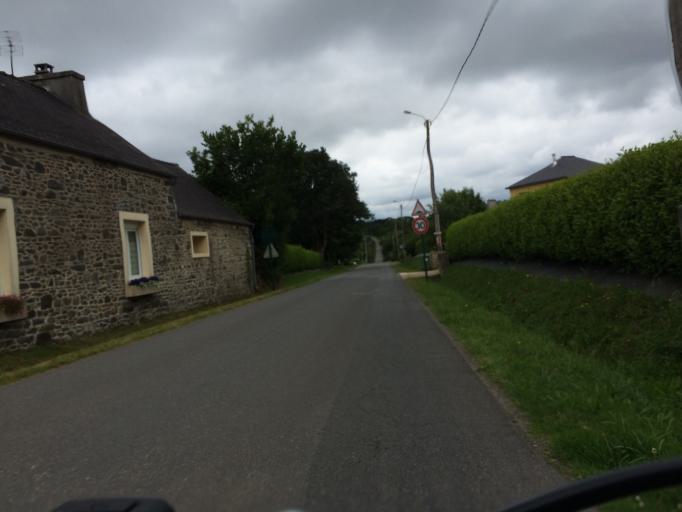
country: FR
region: Brittany
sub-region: Departement du Finistere
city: Hopital-Camfrout
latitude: 48.3301
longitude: -4.2503
